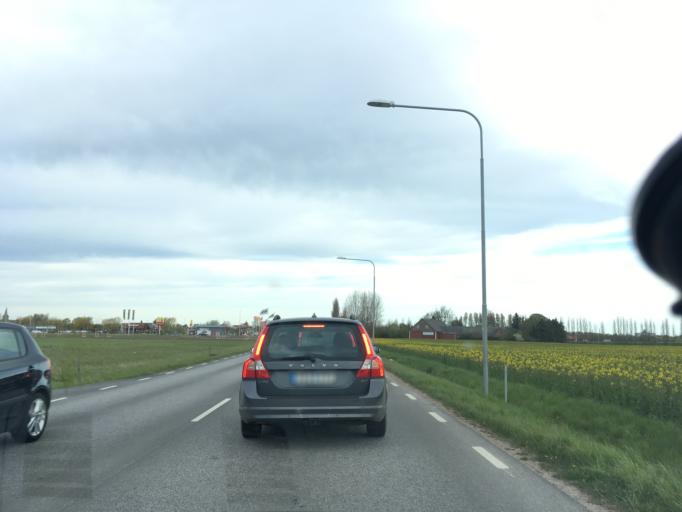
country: SE
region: Skane
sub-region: Lomma Kommun
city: Lomma
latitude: 55.6823
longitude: 13.0945
